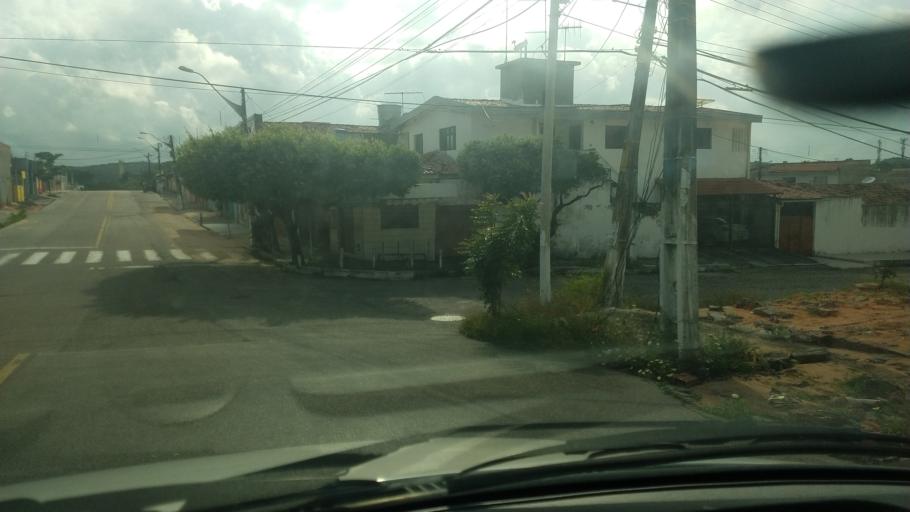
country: BR
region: Rio Grande do Norte
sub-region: Natal
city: Natal
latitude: -5.8425
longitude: -35.2062
